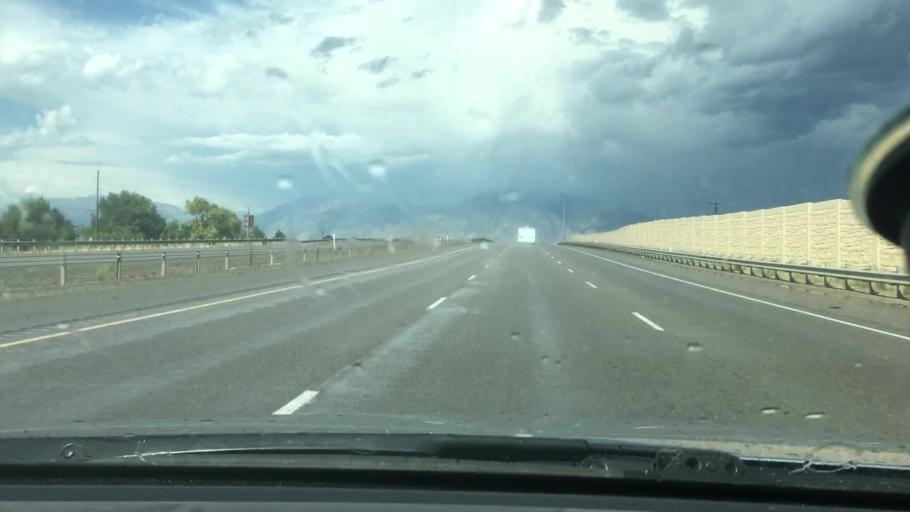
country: US
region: Utah
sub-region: Utah County
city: Payson
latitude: 40.0468
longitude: -111.7415
